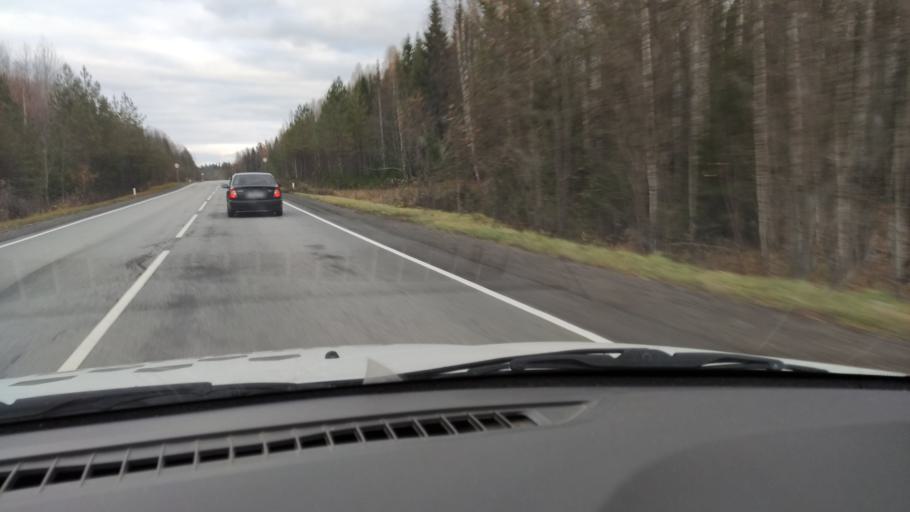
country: RU
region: Kirov
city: Chernaya Kholunitsa
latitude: 58.8666
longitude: 51.5707
